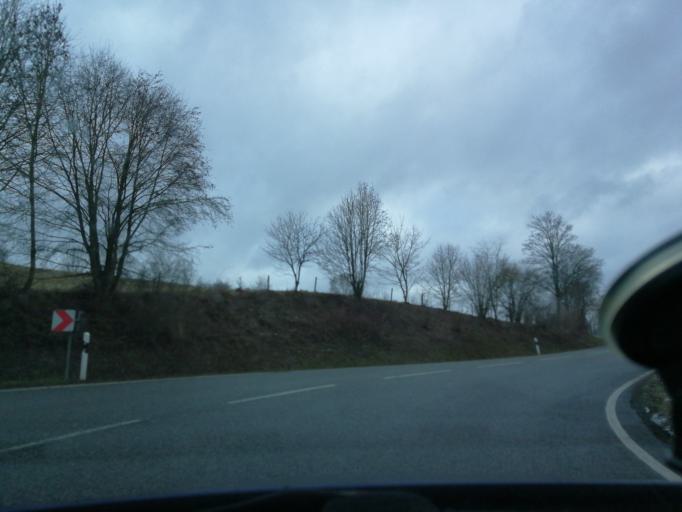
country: DE
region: Rheinland-Pfalz
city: Oberehe-Stroheich
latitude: 50.2783
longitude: 6.7567
